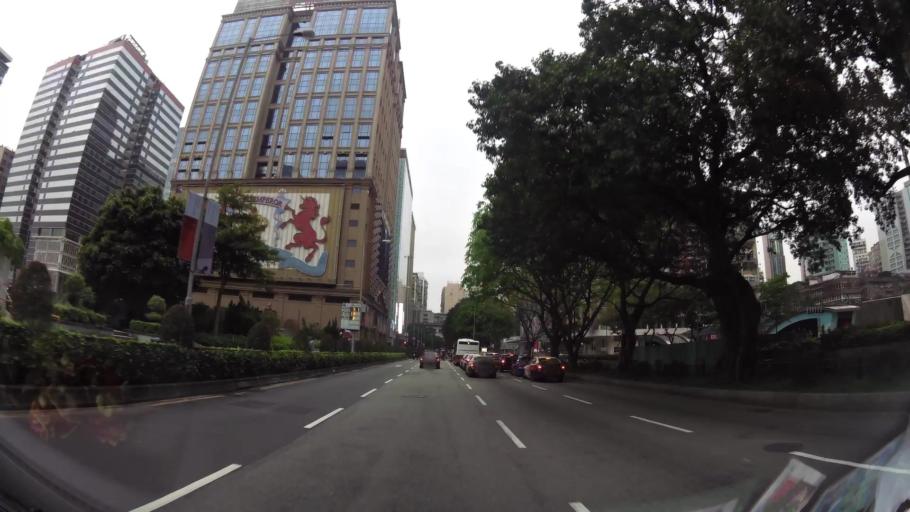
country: MO
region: Macau
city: Macau
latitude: 22.1901
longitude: 113.5418
